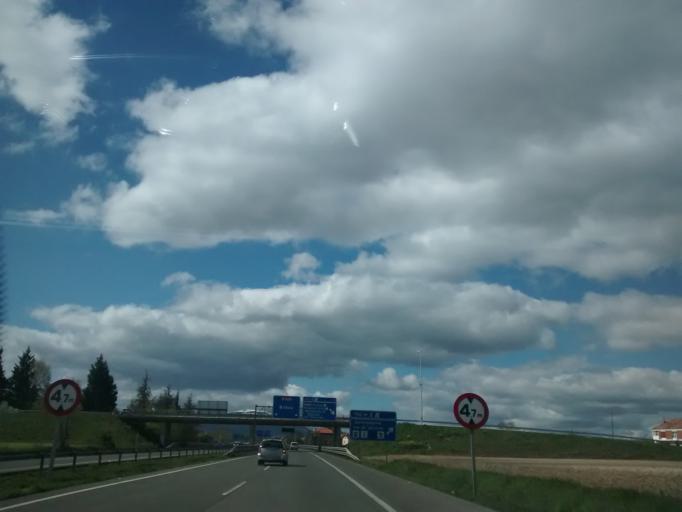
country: ES
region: Basque Country
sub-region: Provincia de Alava
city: Gasteiz / Vitoria
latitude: 42.8868
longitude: -2.6968
